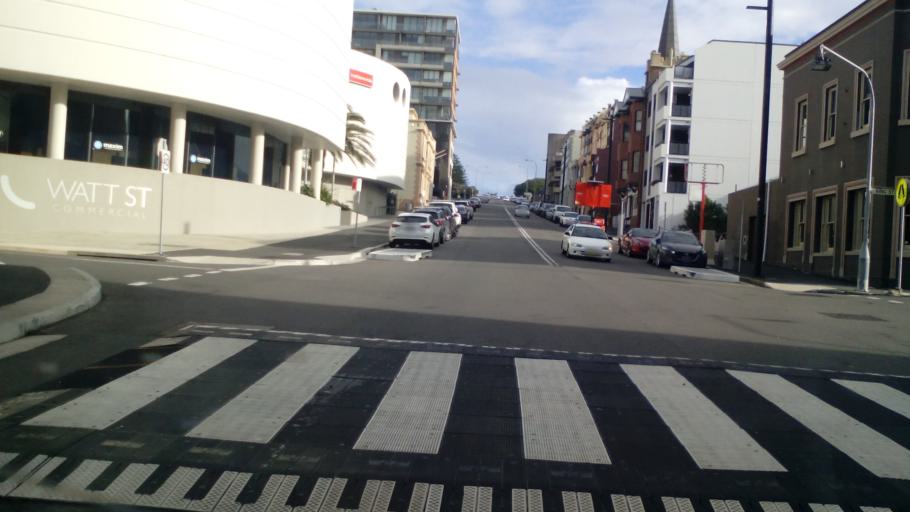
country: AU
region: New South Wales
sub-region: Newcastle
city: Newcastle
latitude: -32.9286
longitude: 151.7840
